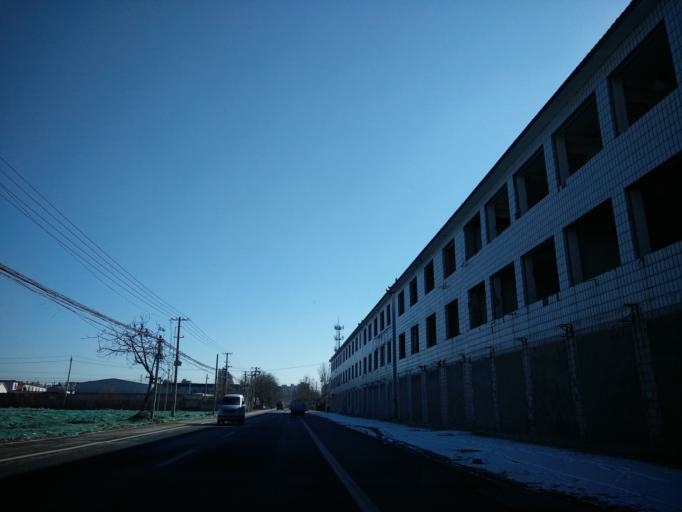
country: CN
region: Beijing
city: Yinghai
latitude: 39.7531
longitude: 116.4652
